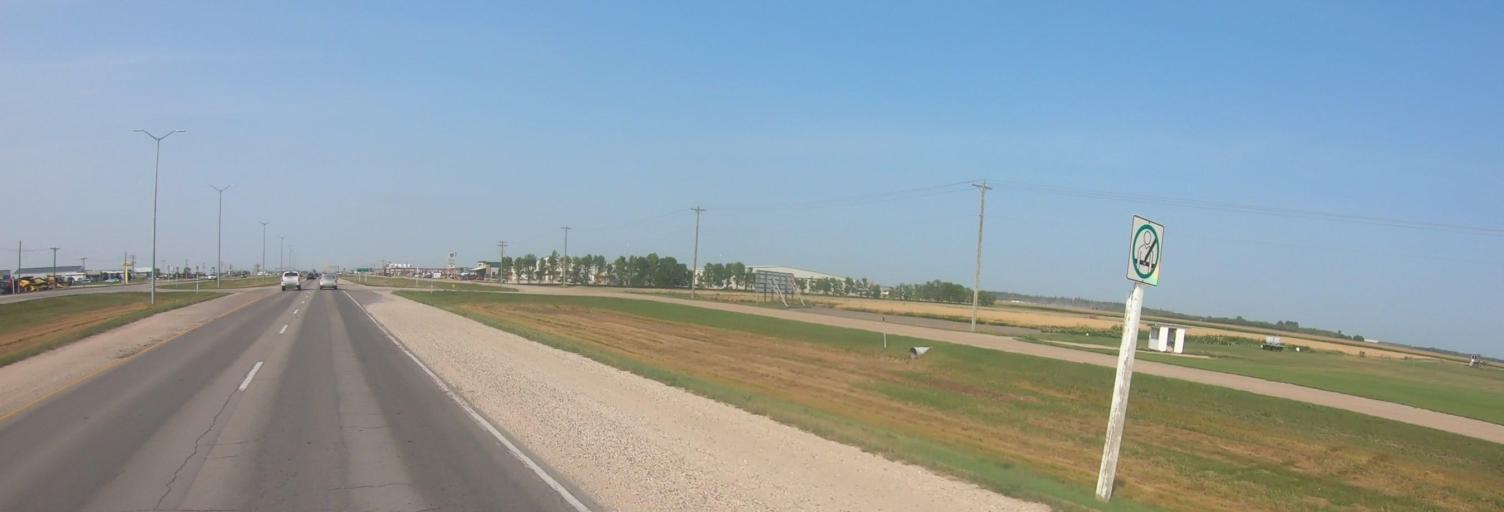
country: CA
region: Manitoba
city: Steinbach
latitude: 49.5527
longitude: -96.6880
